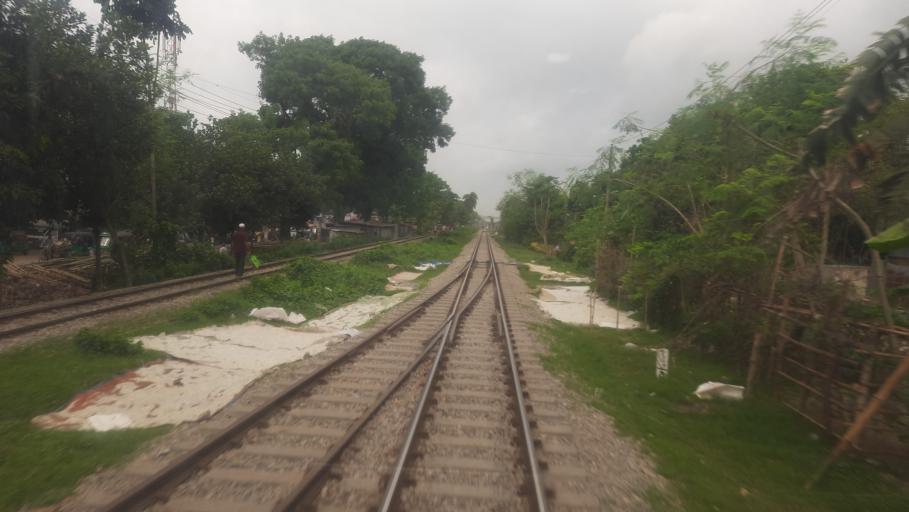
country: BD
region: Dhaka
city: Narsingdi
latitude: 23.9313
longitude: 90.7273
